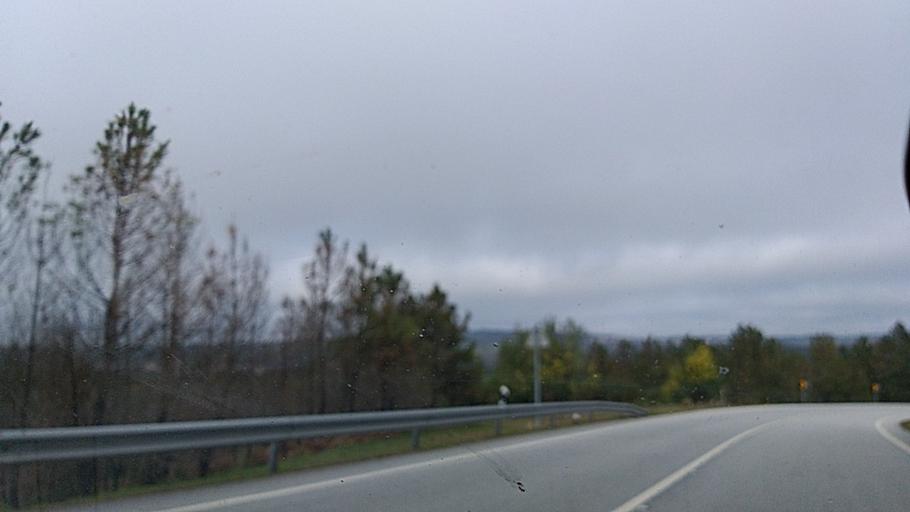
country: PT
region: Guarda
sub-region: Fornos de Algodres
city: Fornos de Algodres
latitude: 40.7104
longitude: -7.4858
